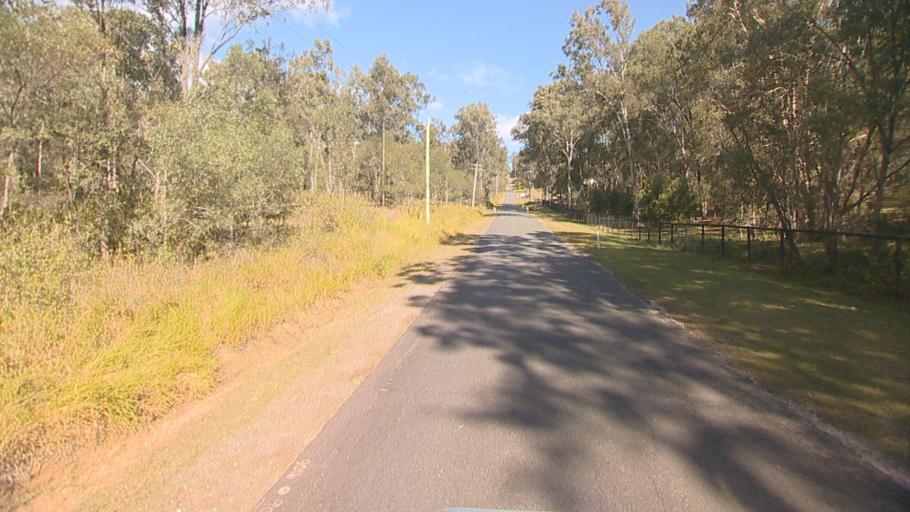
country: AU
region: Queensland
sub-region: Logan
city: Chambers Flat
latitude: -27.8082
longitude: 153.0822
